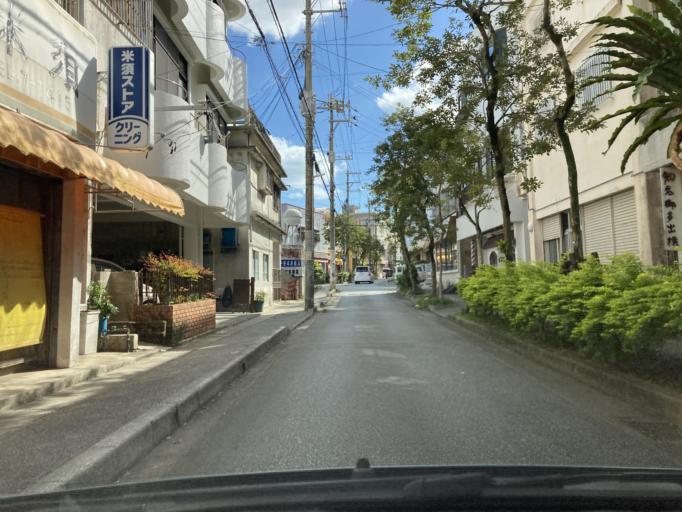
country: JP
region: Okinawa
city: Okinawa
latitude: 26.3386
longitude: 127.8014
